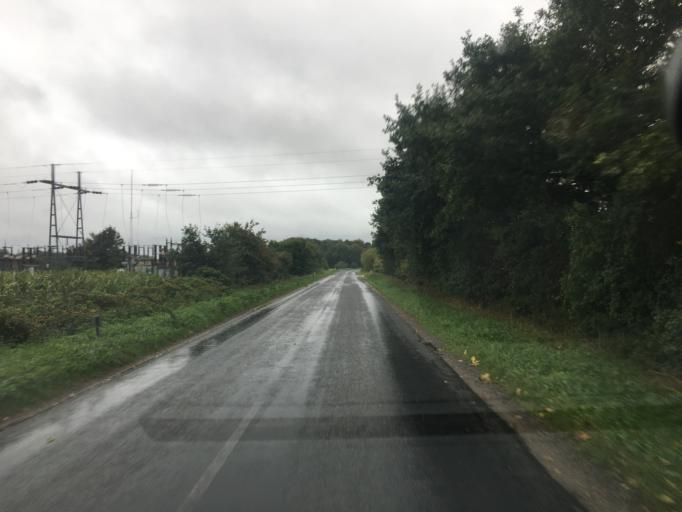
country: DE
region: Schleswig-Holstein
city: Bramstedtlund
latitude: 54.9612
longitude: 9.0515
